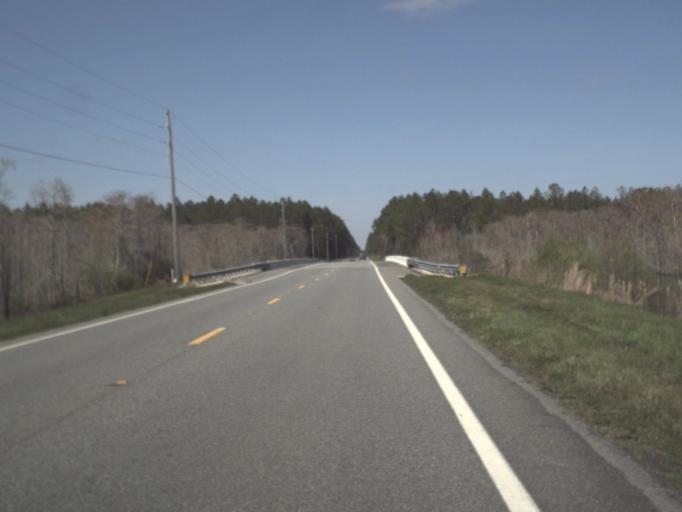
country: US
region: Florida
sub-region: Gulf County
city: Wewahitchka
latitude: 29.9451
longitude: -85.1848
